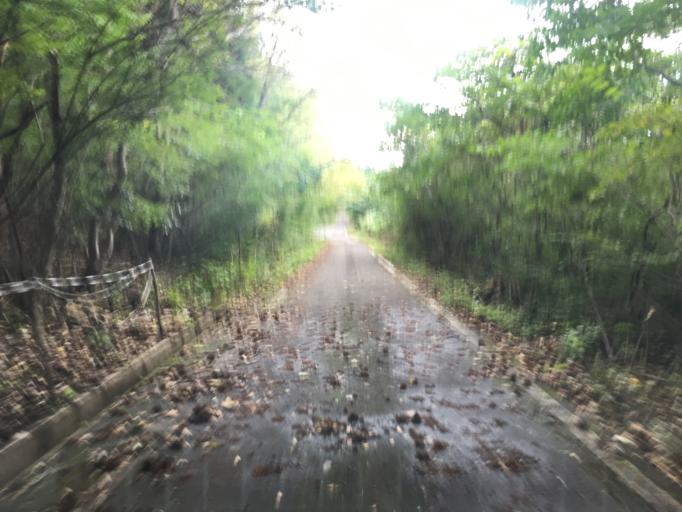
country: JP
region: Miyagi
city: Marumori
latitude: 37.9207
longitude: 140.7167
